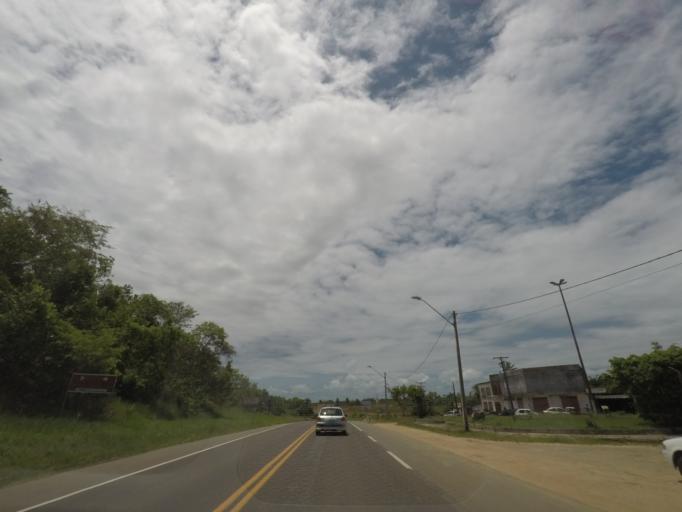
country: BR
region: Bahia
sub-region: Itaparica
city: Itaparica
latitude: -12.9396
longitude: -38.6288
